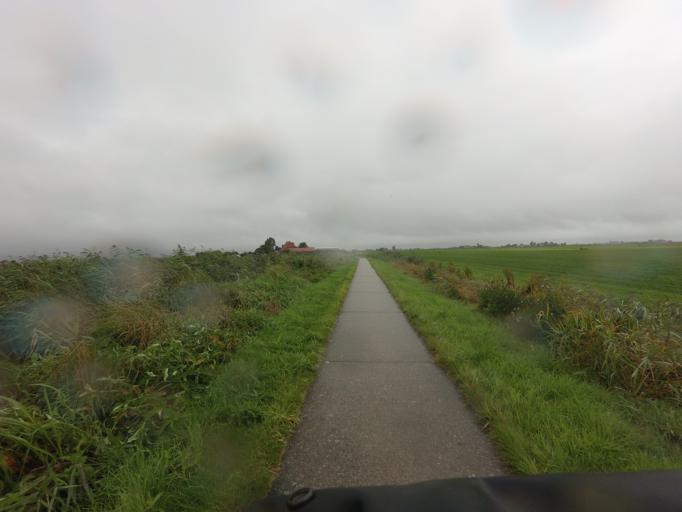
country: NL
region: Friesland
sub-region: Sudwest Fryslan
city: Workum
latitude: 52.9921
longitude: 5.4996
